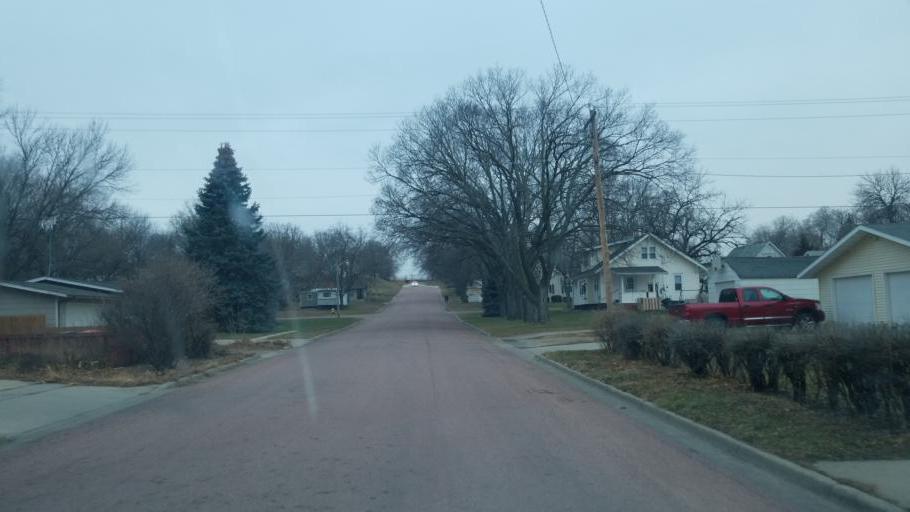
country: US
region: South Dakota
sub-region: Yankton County
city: Yankton
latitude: 42.8752
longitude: -97.4005
